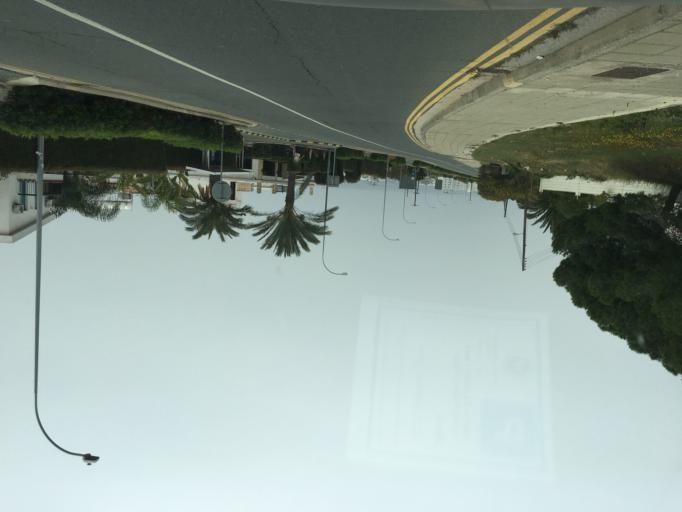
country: CY
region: Ammochostos
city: Ayia Napa
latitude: 34.9934
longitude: 34.0016
